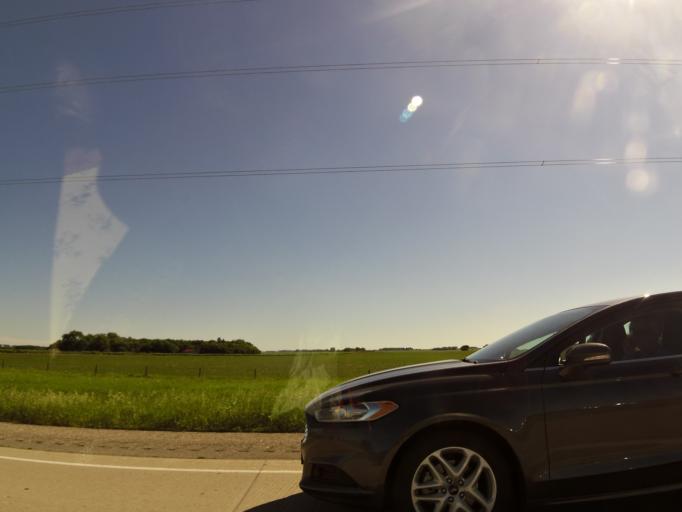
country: US
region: Minnesota
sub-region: Clay County
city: Barnesville
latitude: 46.5497
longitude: -96.3098
